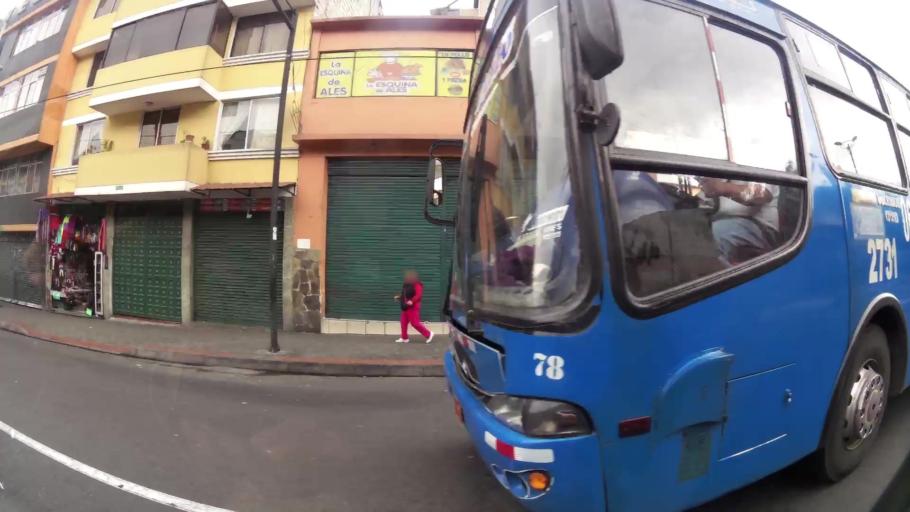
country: EC
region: Pichincha
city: Quito
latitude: -0.2260
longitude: -78.5068
